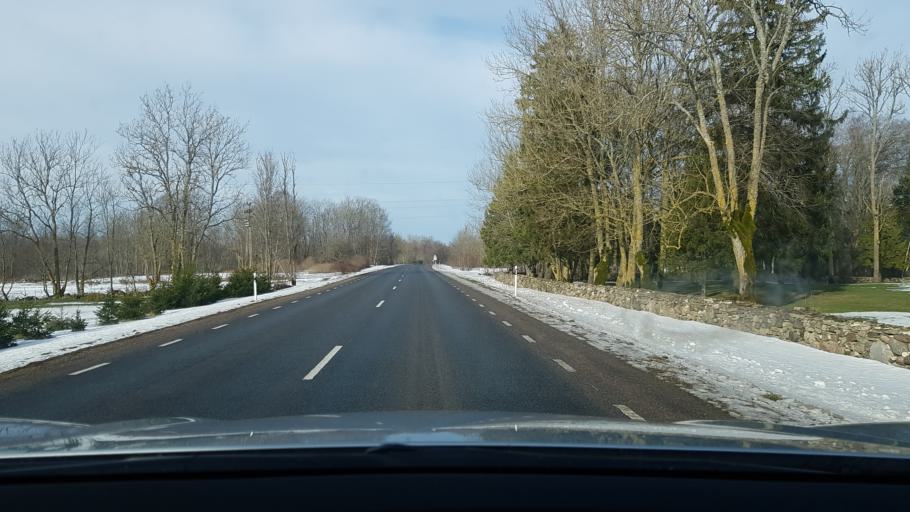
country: EE
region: Saare
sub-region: Kuressaare linn
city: Kuressaare
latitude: 58.2971
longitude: 22.5412
